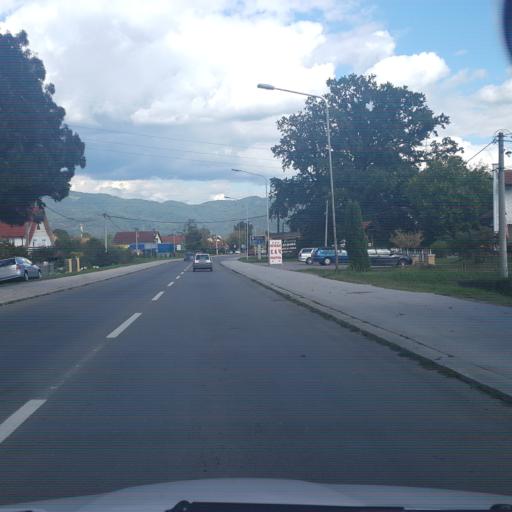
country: RS
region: Central Serbia
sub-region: Raski Okrug
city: Vrnjacka Banja
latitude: 43.6304
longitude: 20.9018
